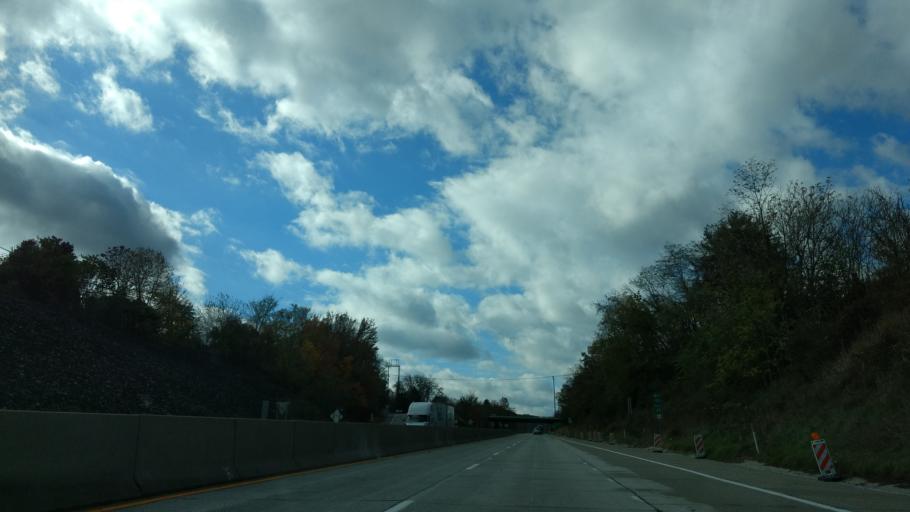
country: US
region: Pennsylvania
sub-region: Washington County
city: Speers
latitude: 40.1218
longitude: -79.8829
